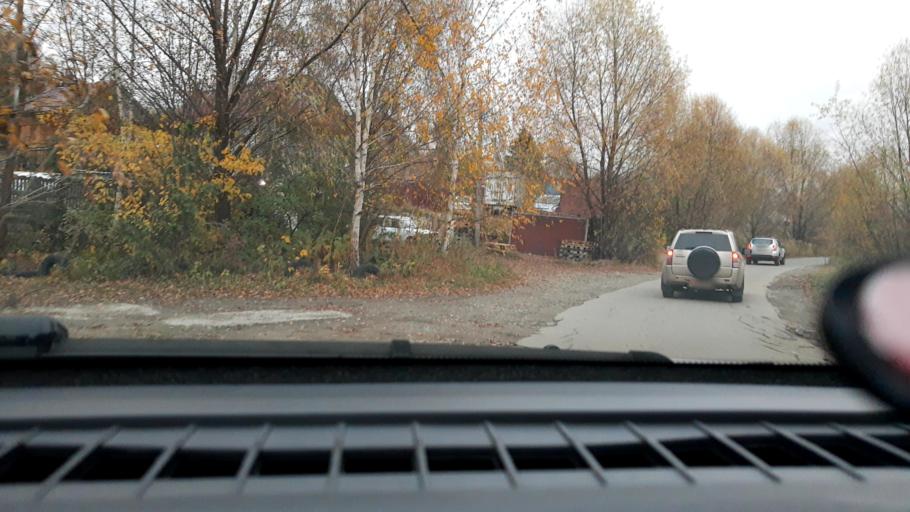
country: RU
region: Nizjnij Novgorod
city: Nizhniy Novgorod
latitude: 56.2527
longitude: 43.9882
